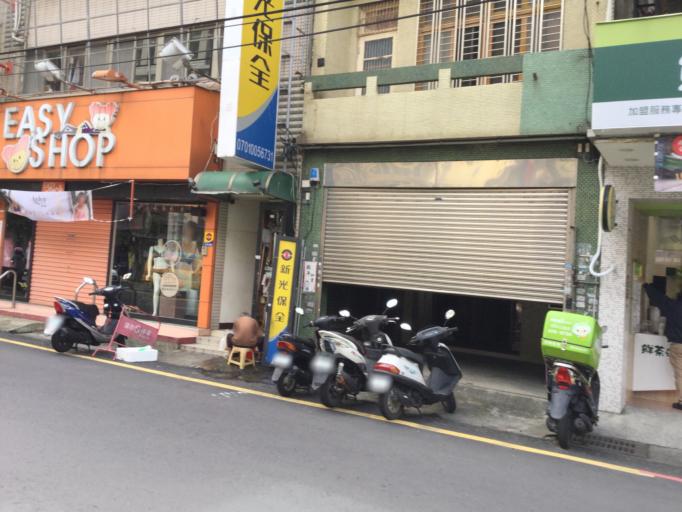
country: TW
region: Taiwan
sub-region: Hsinchu
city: Hsinchu
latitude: 24.7842
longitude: 121.0154
